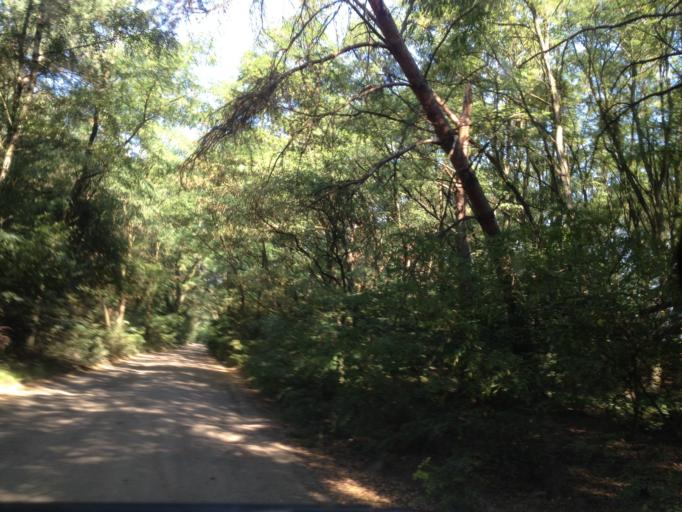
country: PL
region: Greater Poland Voivodeship
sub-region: Powiat sredzki
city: Zaniemysl
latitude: 52.1096
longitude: 17.1225
